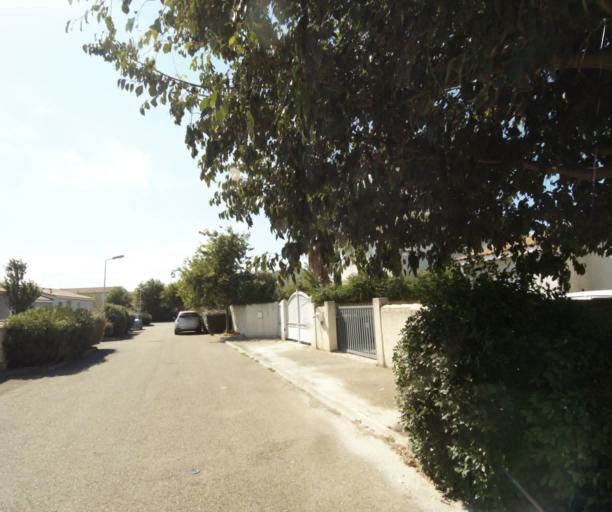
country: FR
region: Languedoc-Roussillon
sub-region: Departement du Gard
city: Bouillargues
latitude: 43.8049
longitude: 4.4339
